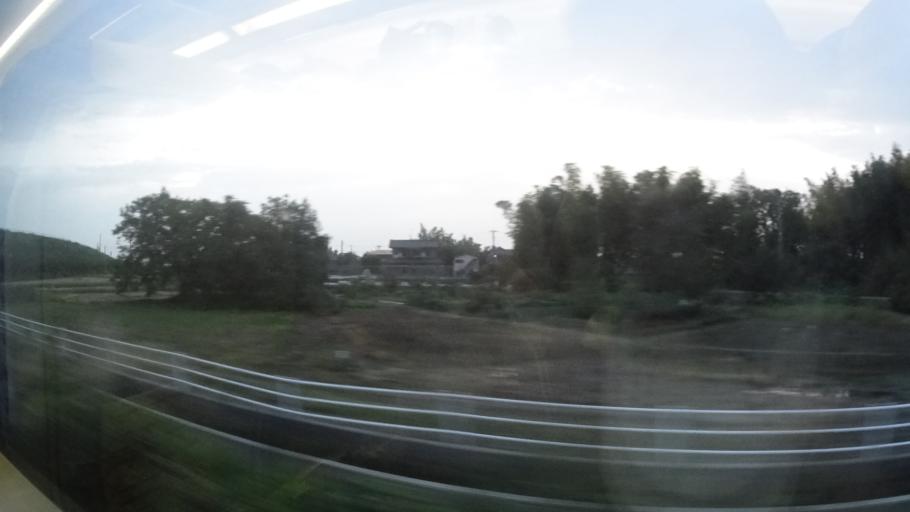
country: JP
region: Niigata
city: Shibata
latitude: 38.0357
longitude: 139.3884
